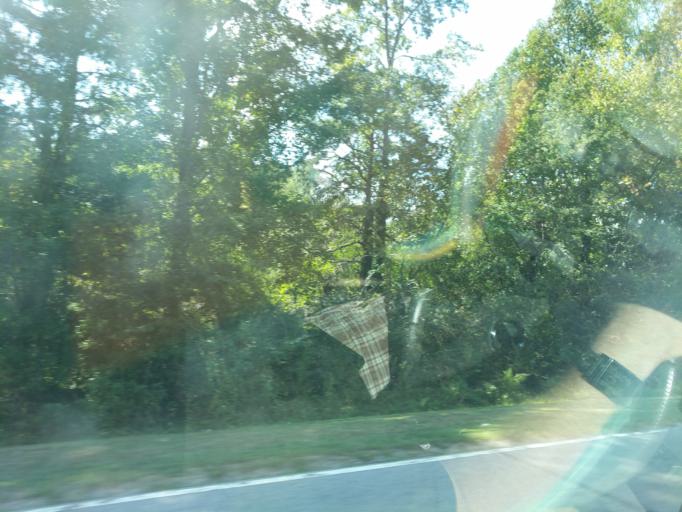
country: US
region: South Carolina
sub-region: Greenville County
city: Fountain Inn
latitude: 34.5993
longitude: -82.1077
